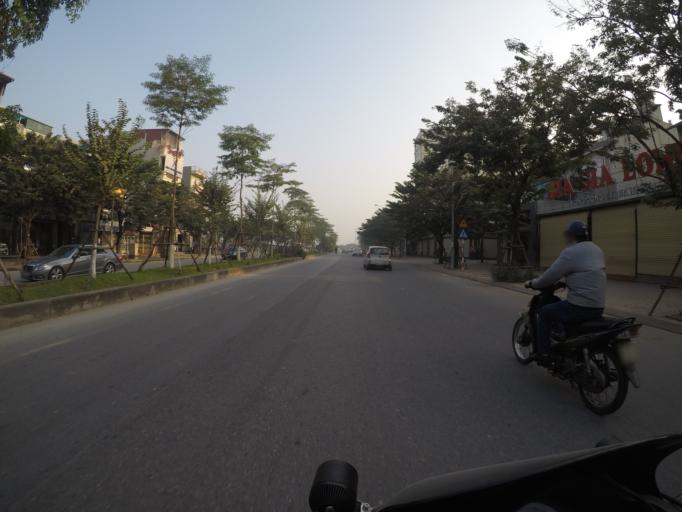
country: VN
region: Ha Noi
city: Trau Quy
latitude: 21.0396
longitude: 105.9041
